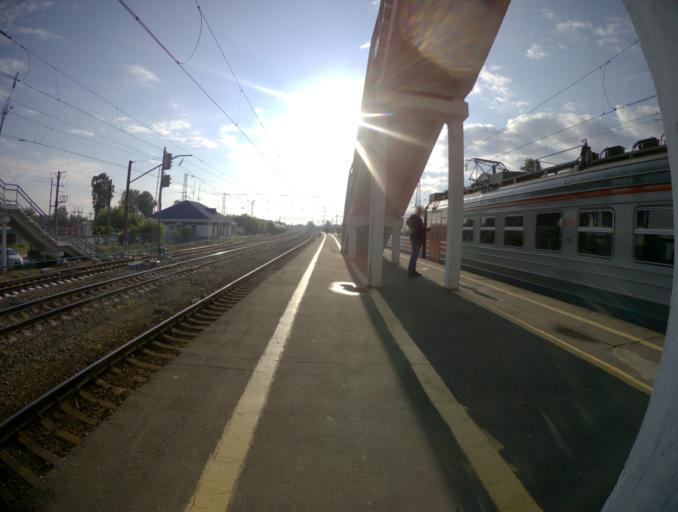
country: RU
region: Vladimir
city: Galitsy
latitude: 56.1592
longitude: 42.8136
